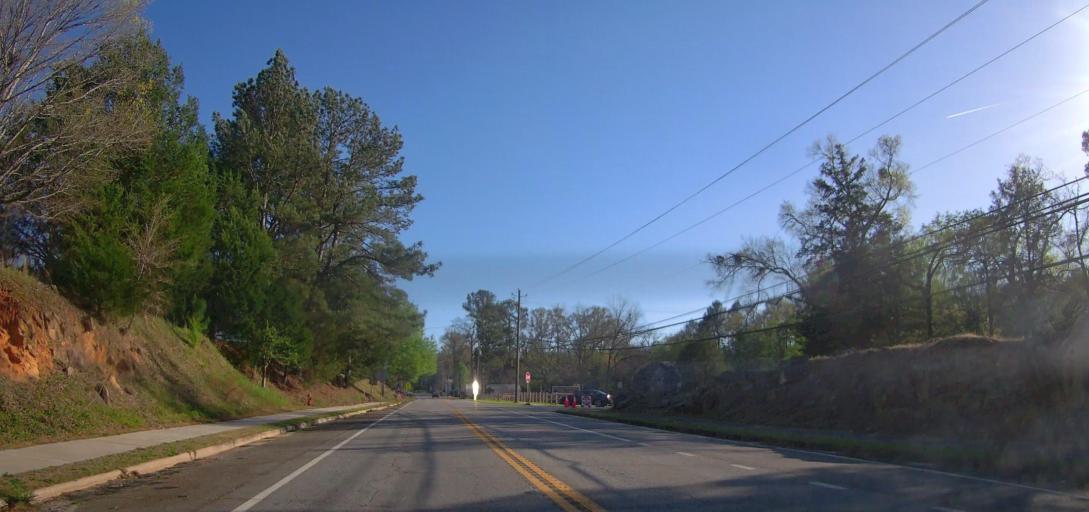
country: US
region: Georgia
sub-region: Butts County
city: Indian Springs
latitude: 33.2456
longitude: -83.9204
